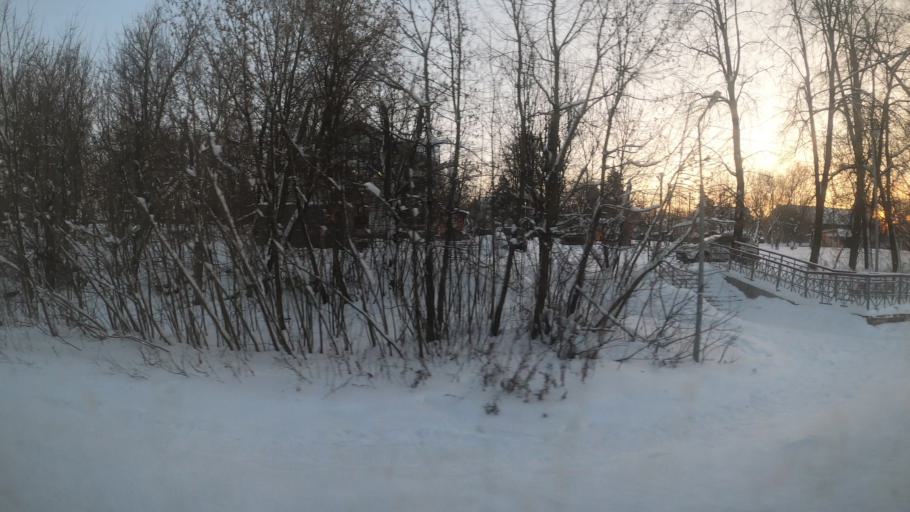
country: RU
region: Moskovskaya
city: Dedenevo
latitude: 56.2427
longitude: 37.5122
